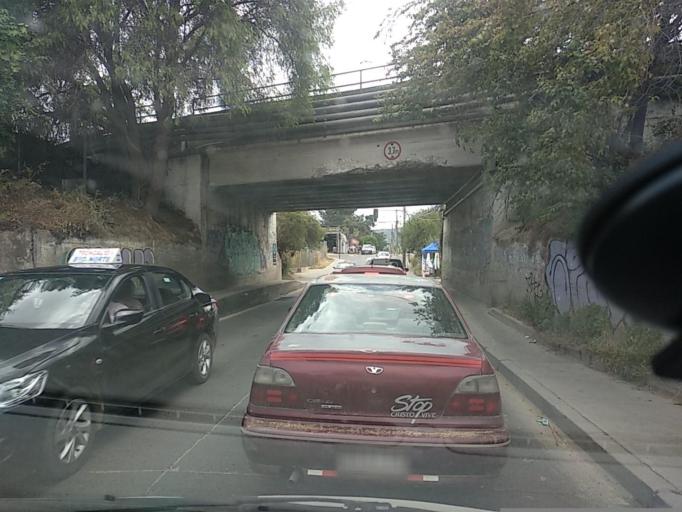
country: CL
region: Valparaiso
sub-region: Provincia de Marga Marga
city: Villa Alemana
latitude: -33.0437
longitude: -71.4053
